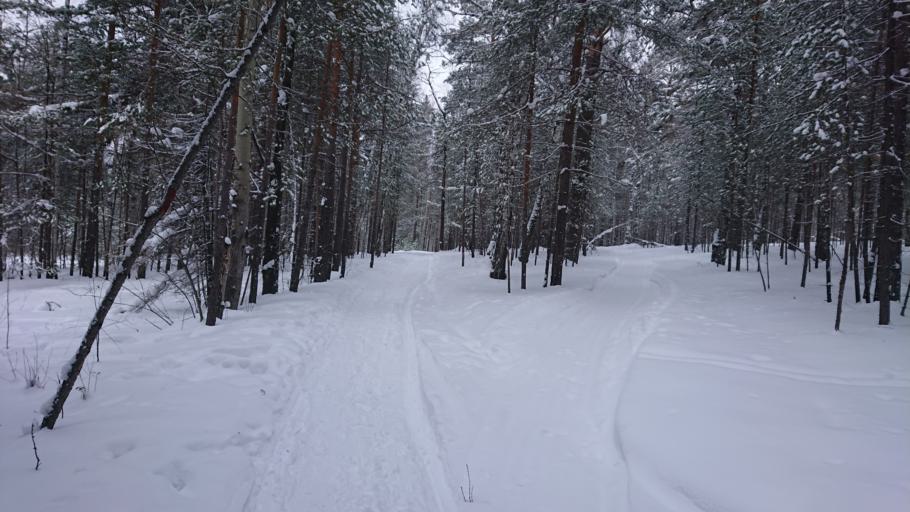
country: RU
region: Sverdlovsk
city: Degtyarsk
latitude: 56.6926
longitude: 60.0656
